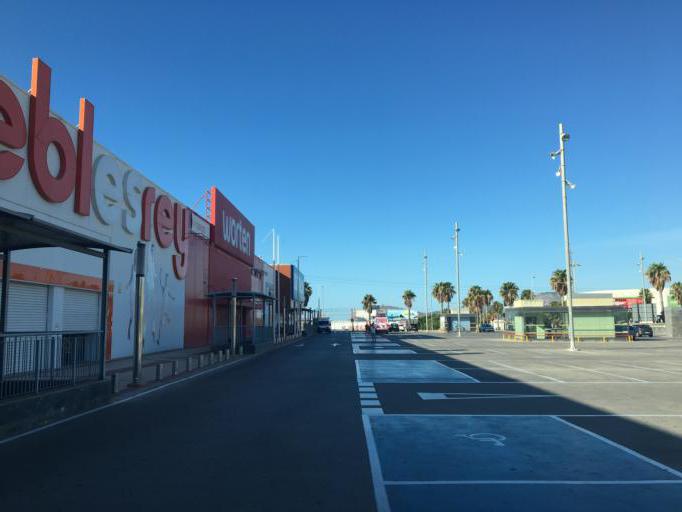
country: ES
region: Murcia
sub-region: Murcia
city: Cartagena
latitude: 37.6238
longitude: -0.9491
